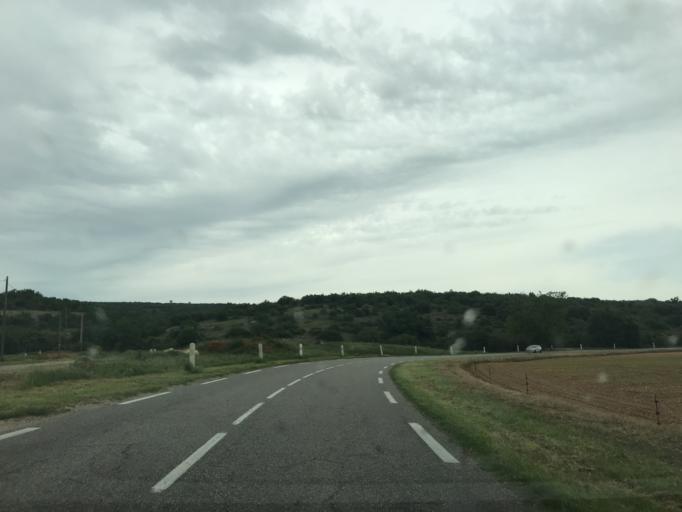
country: FR
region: Provence-Alpes-Cote d'Azur
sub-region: Departement du Var
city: Ginasservis
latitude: 43.6416
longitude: 5.8059
